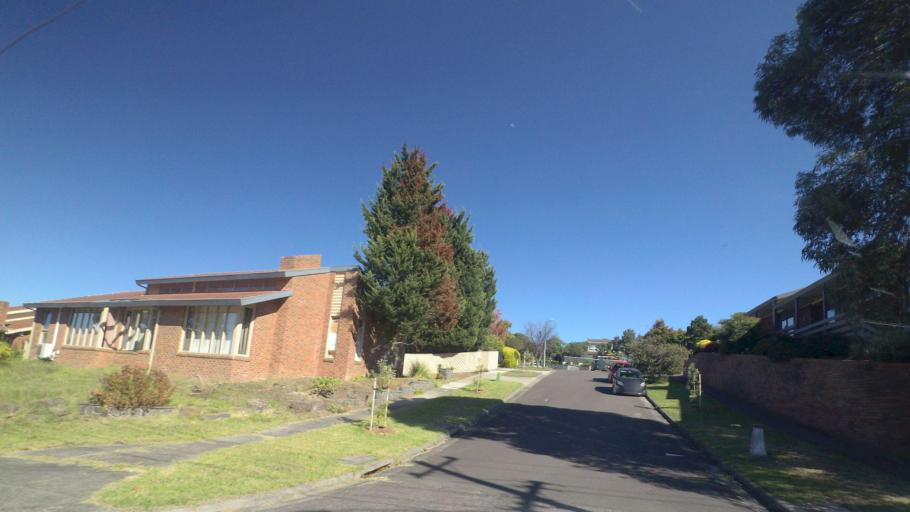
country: AU
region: Victoria
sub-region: Manningham
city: Donvale
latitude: -37.7779
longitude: 145.1777
